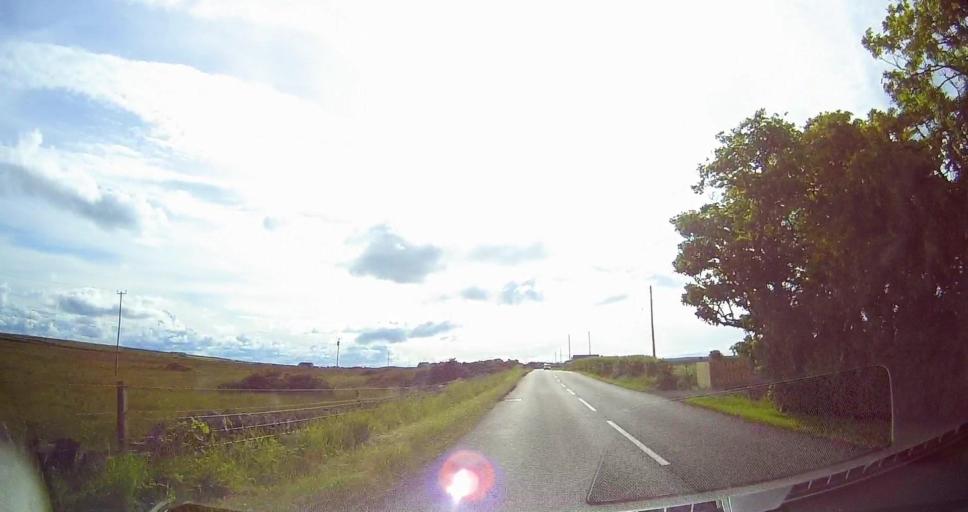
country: GB
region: Scotland
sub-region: Highland
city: Thurso
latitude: 58.6291
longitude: -3.3063
